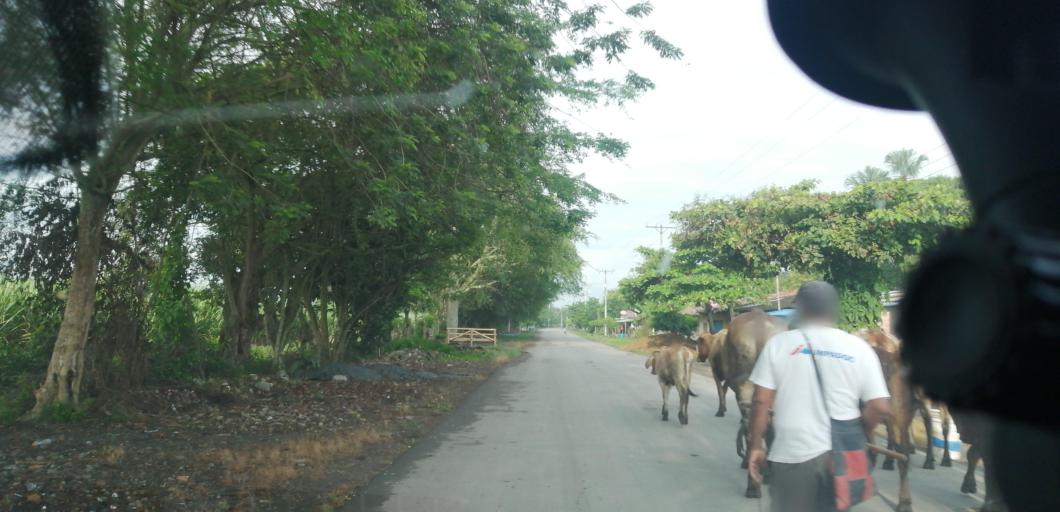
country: CO
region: Valle del Cauca
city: Palmira
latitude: 3.5369
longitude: -76.3568
